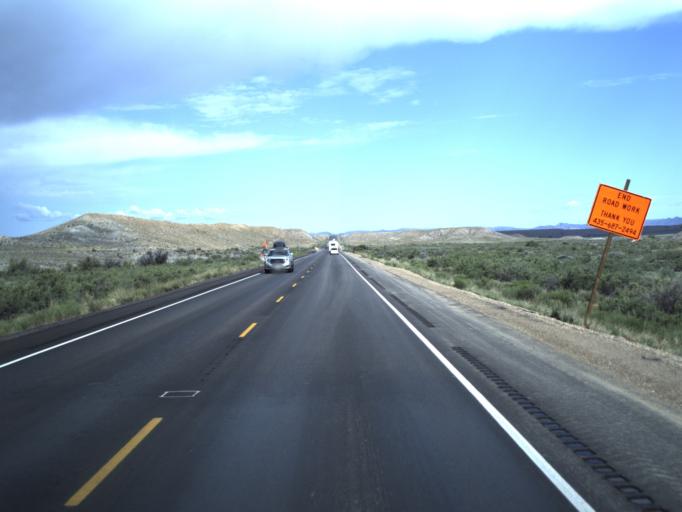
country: US
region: Utah
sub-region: Carbon County
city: East Carbon City
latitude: 39.4650
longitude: -110.4920
